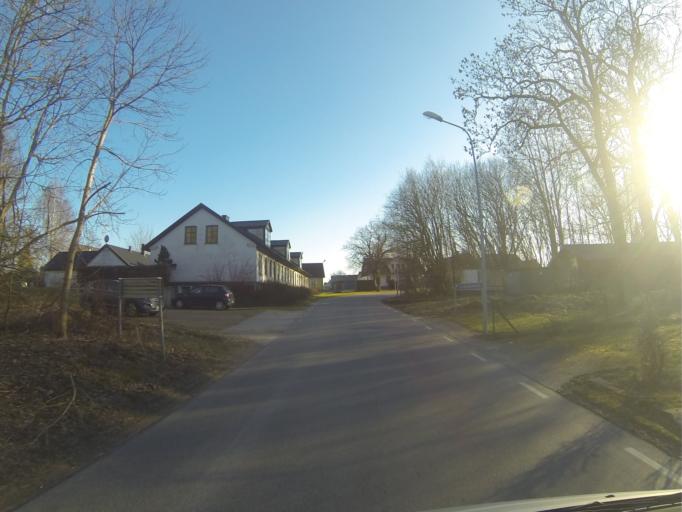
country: SE
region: Skane
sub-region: Horby Kommun
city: Hoerby
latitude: 55.8378
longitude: 13.6241
